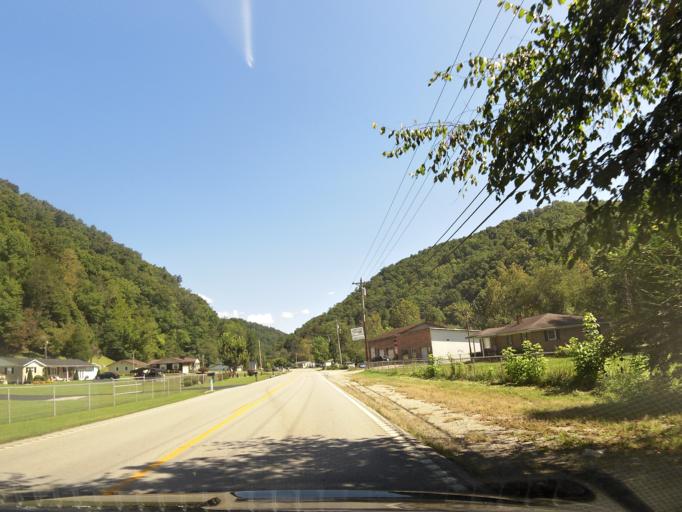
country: US
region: Kentucky
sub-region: Clay County
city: Manchester
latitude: 37.1424
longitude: -83.6088
